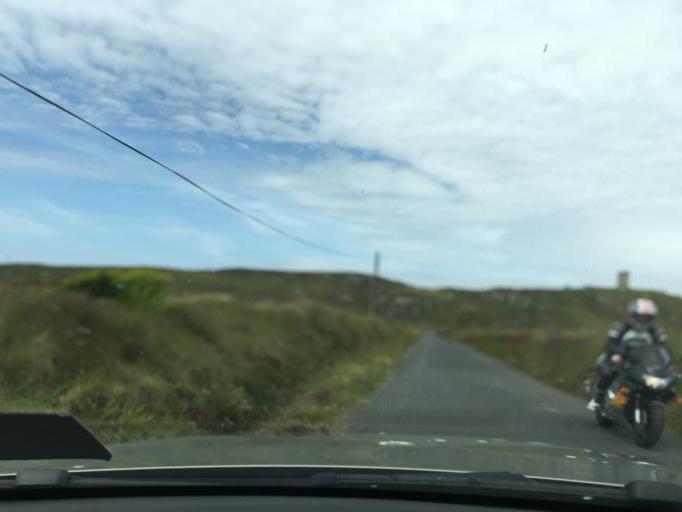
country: IE
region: Ulster
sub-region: County Donegal
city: Carndonagh
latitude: 55.3776
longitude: -7.3706
